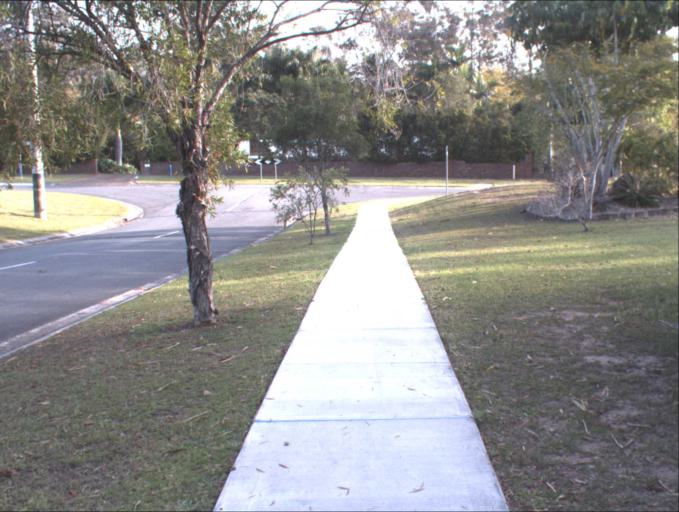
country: AU
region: Queensland
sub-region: Logan
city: Park Ridge South
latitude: -27.6768
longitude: 153.0132
